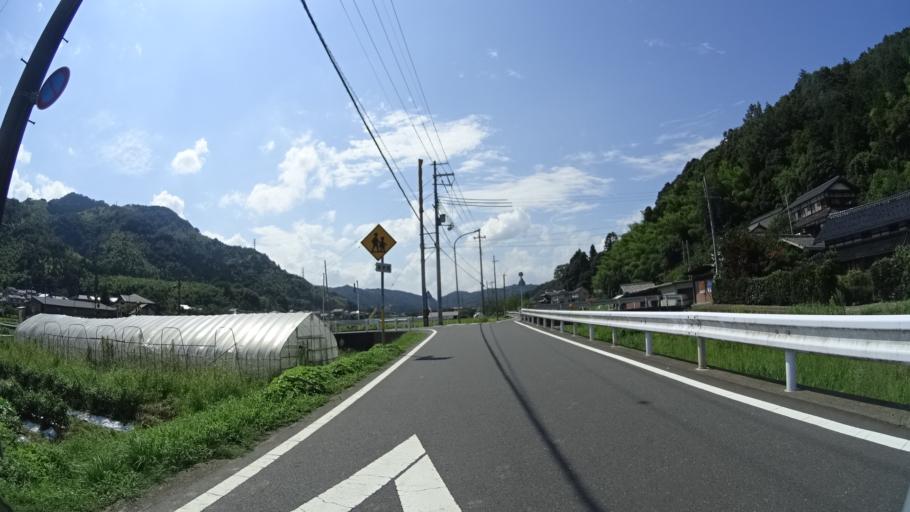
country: JP
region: Kyoto
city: Maizuru
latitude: 35.4313
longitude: 135.3147
